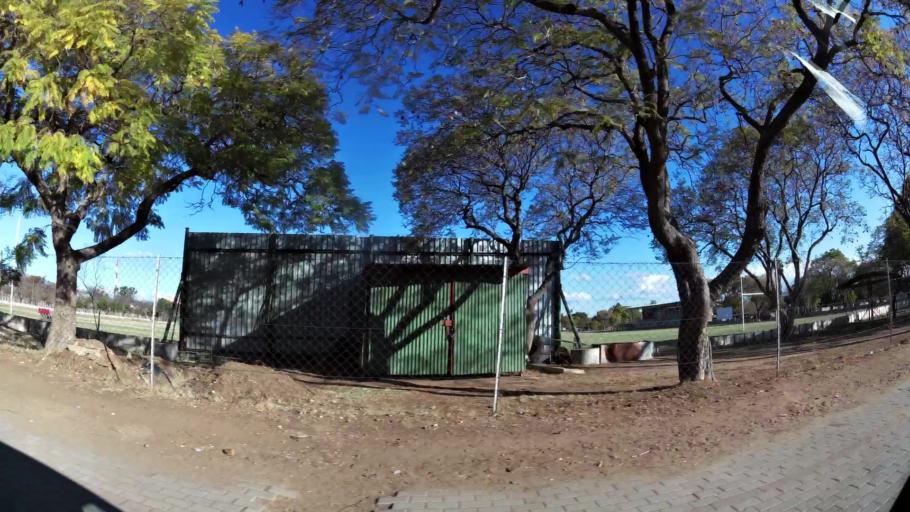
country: ZA
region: Limpopo
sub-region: Capricorn District Municipality
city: Polokwane
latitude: -23.8971
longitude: 29.4562
